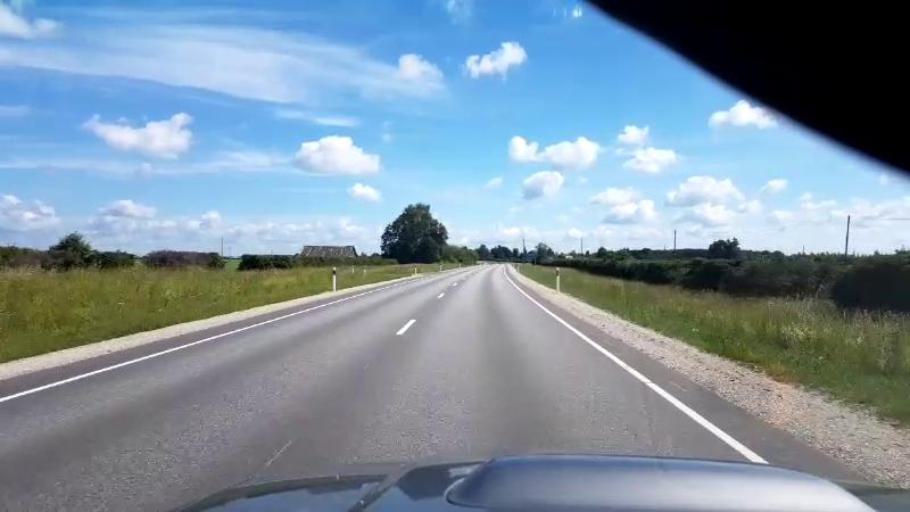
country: EE
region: Jaervamaa
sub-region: Jaerva-Jaani vald
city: Jarva-Jaani
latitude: 59.1048
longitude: 25.7128
